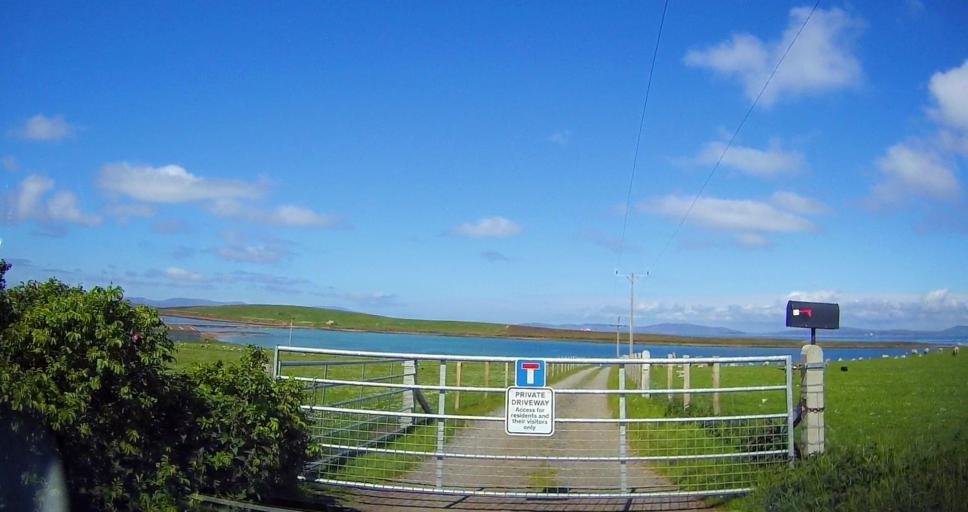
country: GB
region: Scotland
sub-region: Orkney Islands
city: Orkney
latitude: 58.8524
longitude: -2.9543
